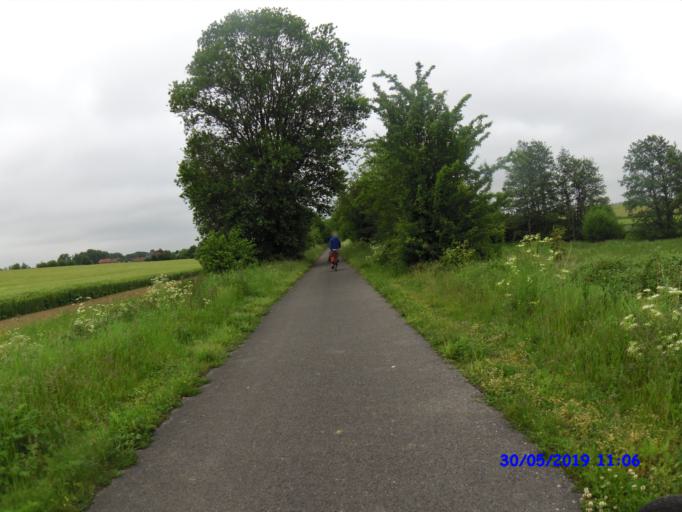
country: BE
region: Wallonia
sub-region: Province du Hainaut
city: Thuin
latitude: 50.2869
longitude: 4.3267
